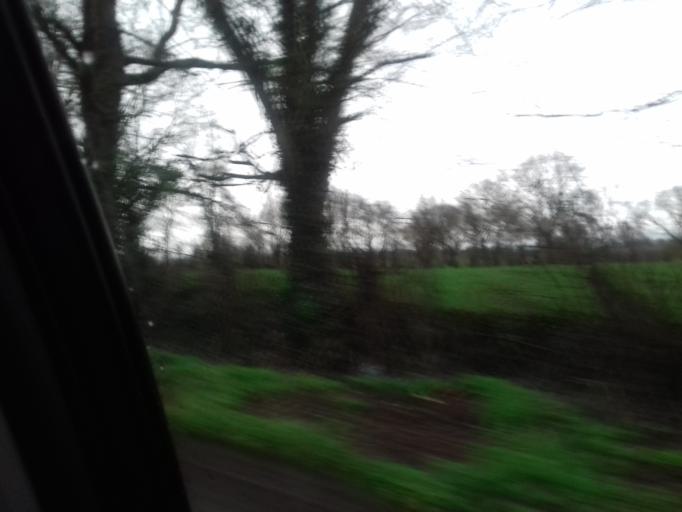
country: IE
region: Leinster
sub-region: County Carlow
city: Bagenalstown
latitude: 52.6725
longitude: -7.0114
